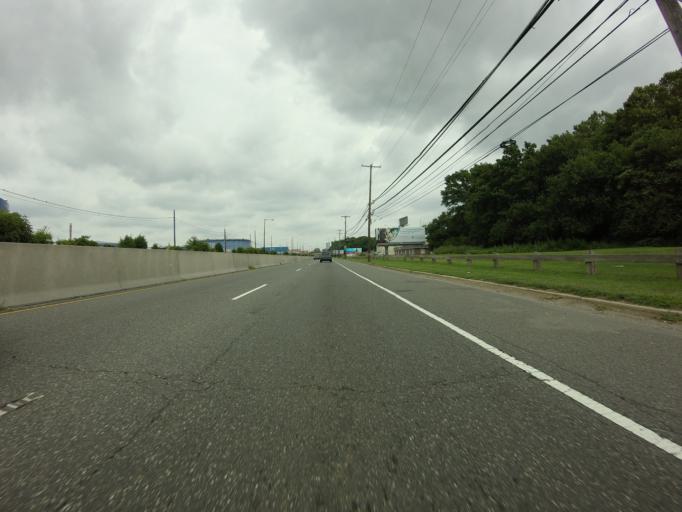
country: US
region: New Jersey
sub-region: Gloucester County
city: National Park
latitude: 39.9128
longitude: -75.1924
